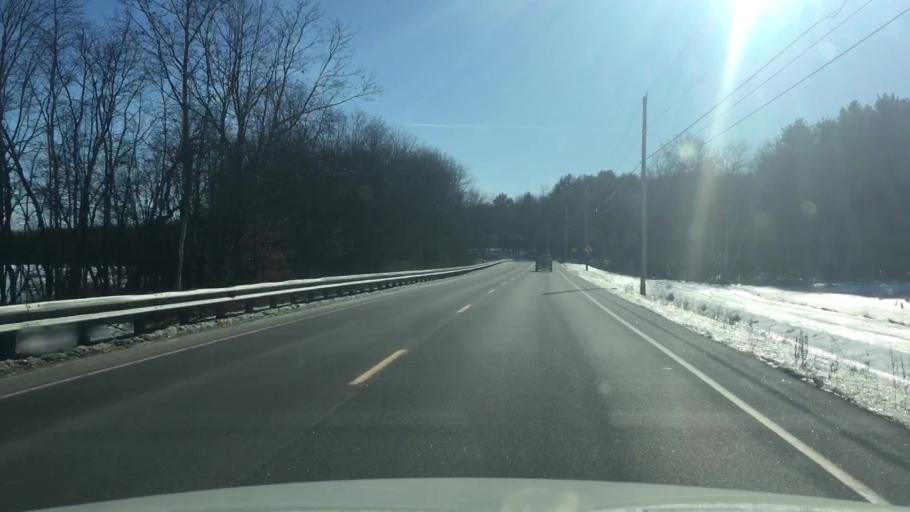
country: US
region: Maine
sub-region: Androscoggin County
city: Lisbon
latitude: 43.9883
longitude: -70.1375
